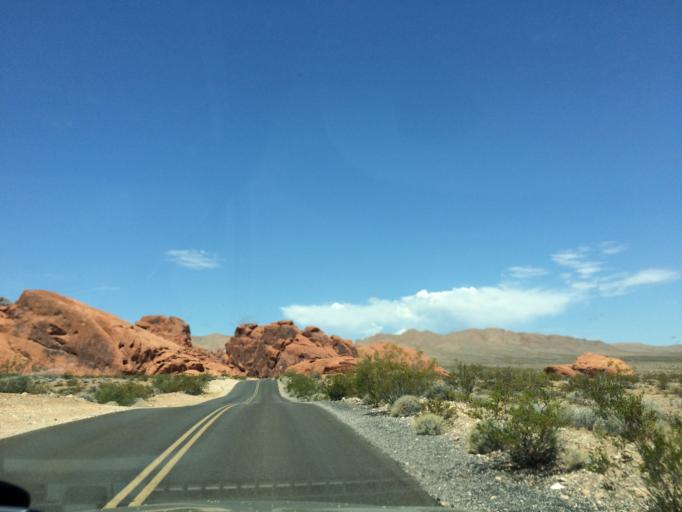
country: US
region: Nevada
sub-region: Clark County
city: Moapa Valley
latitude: 36.4217
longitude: -114.5454
